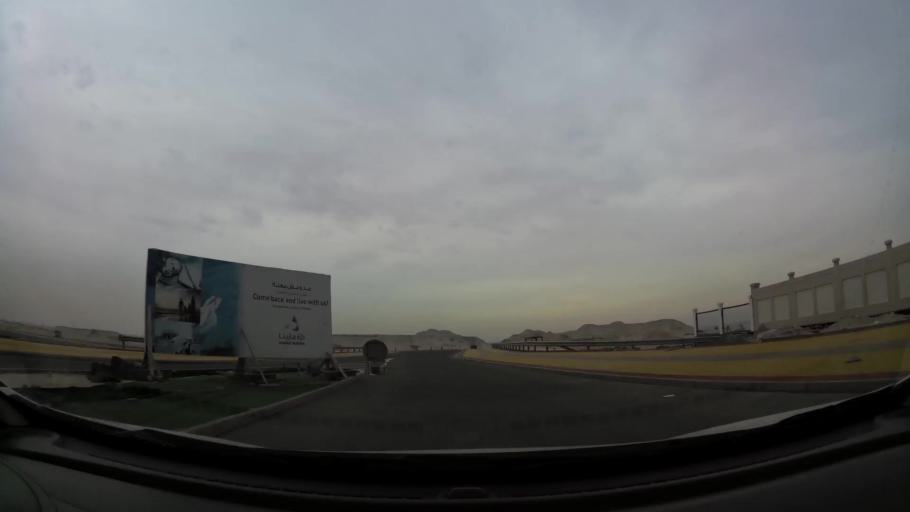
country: BH
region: Central Governorate
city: Dar Kulayb
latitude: 25.8687
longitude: 50.6070
